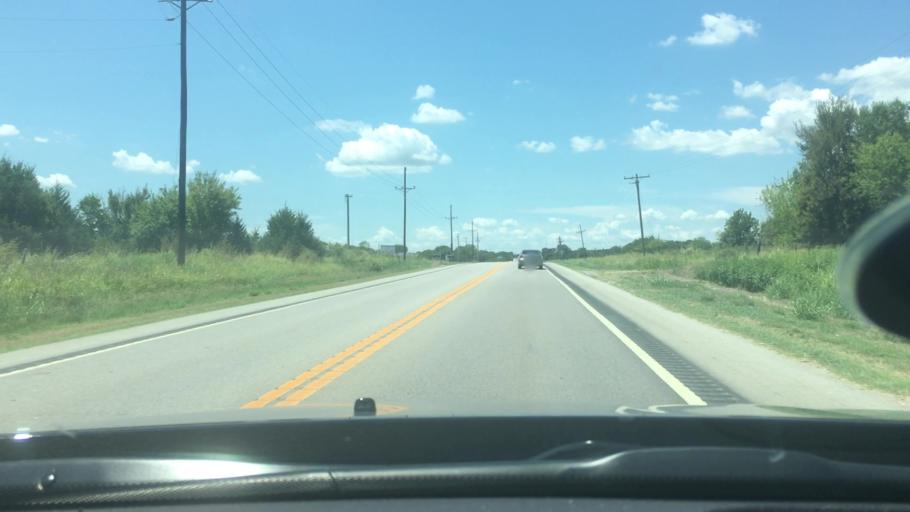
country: US
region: Oklahoma
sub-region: Bryan County
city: Durant
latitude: 33.9975
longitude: -96.3231
